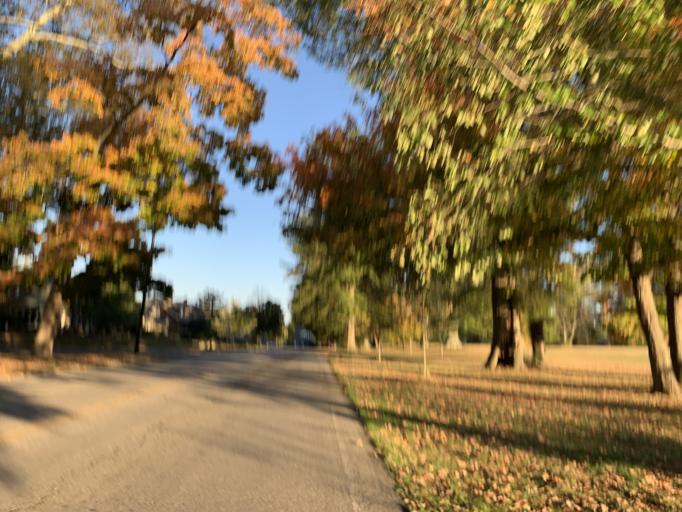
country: US
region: Indiana
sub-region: Floyd County
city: New Albany
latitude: 38.2607
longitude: -85.8258
